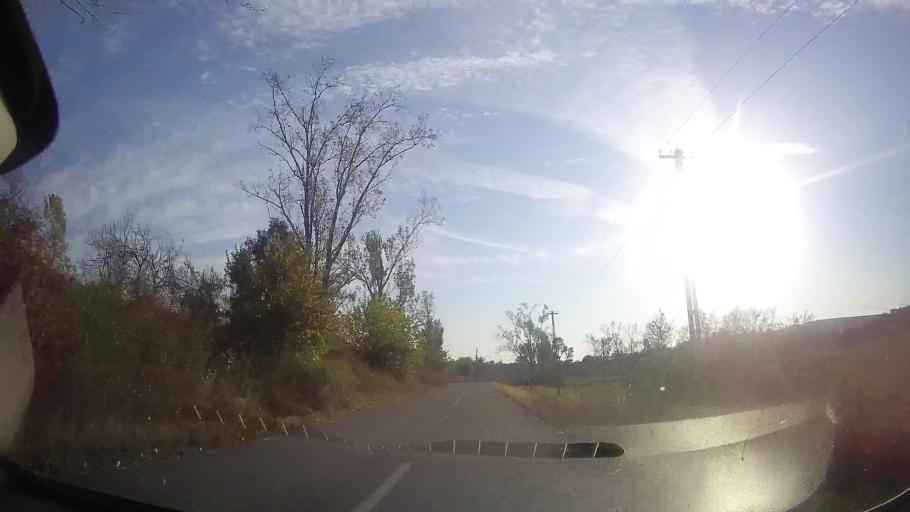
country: RO
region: Timis
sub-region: Comuna Bogda
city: Bogda
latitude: 45.9804
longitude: 21.5115
